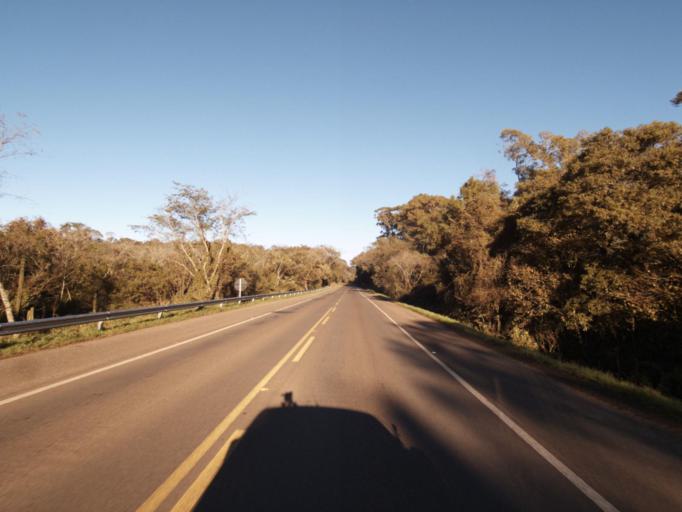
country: BR
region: Santa Catarina
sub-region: Sao Lourenco Do Oeste
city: Sao Lourenco dOeste
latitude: -26.7644
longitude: -53.2543
